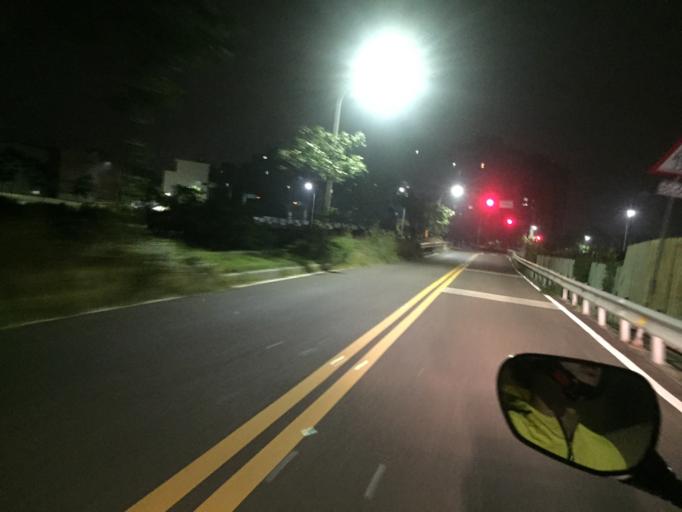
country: TW
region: Taiwan
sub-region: Hsinchu
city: Hsinchu
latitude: 24.8013
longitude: 120.9495
